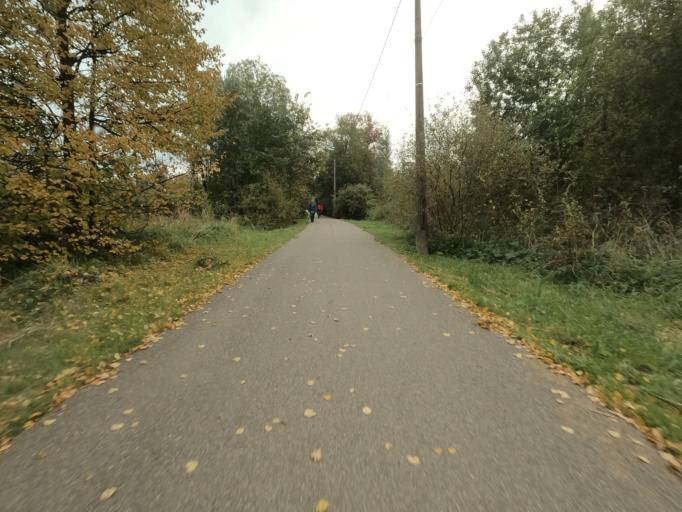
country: RU
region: St.-Petersburg
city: Pontonnyy
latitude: 59.7879
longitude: 30.6180
